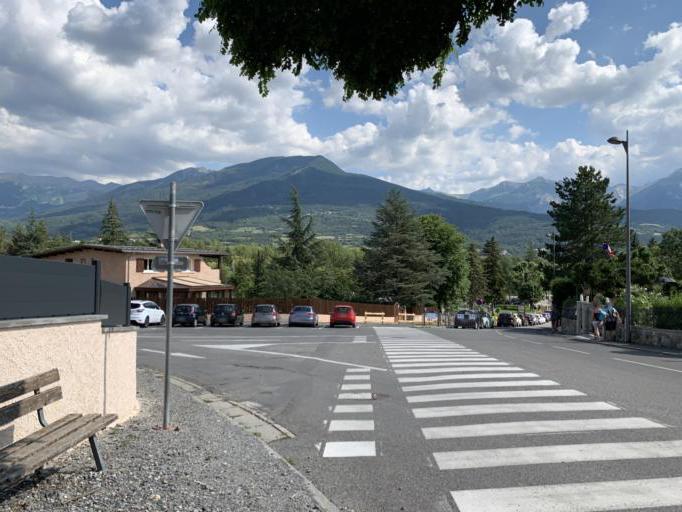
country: FR
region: Provence-Alpes-Cote d'Azur
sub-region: Departement des Hautes-Alpes
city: Embrun
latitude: 44.5521
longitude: 6.4795
